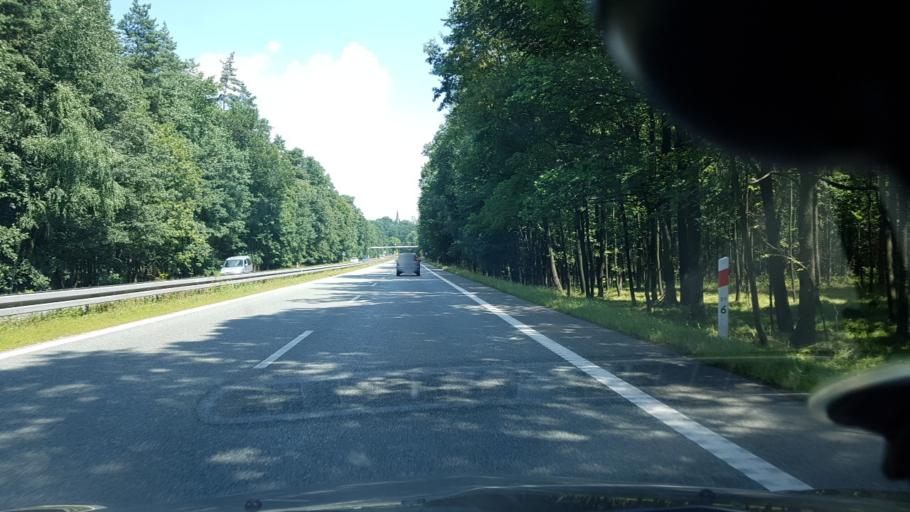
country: PL
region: Silesian Voivodeship
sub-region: Powiat pszczynski
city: Rudziczka
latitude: 50.0753
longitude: 18.7462
